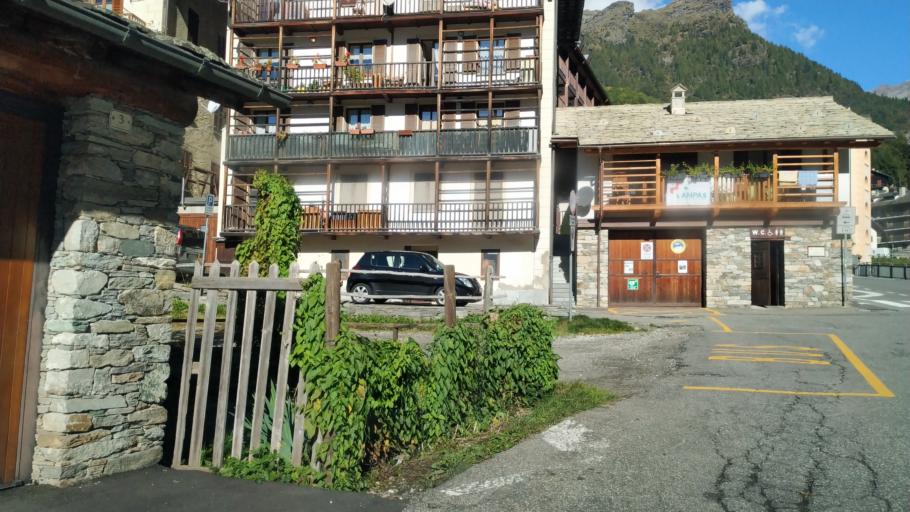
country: IT
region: Piedmont
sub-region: Provincia di Vercelli
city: Alagna Valsesia
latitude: 45.8541
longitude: 7.9381
